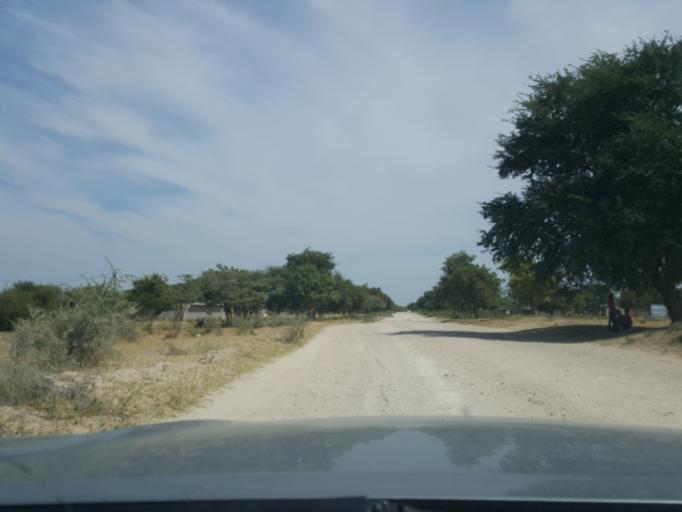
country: BW
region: North West
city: Shakawe
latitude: -18.3156
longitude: 21.9022
